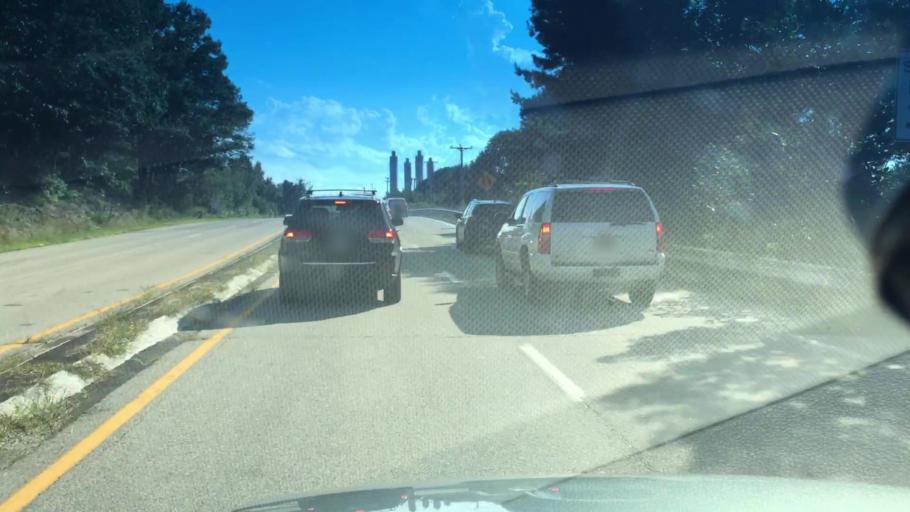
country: US
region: Maine
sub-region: York County
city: Kittery
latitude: 43.0922
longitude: -70.7550
